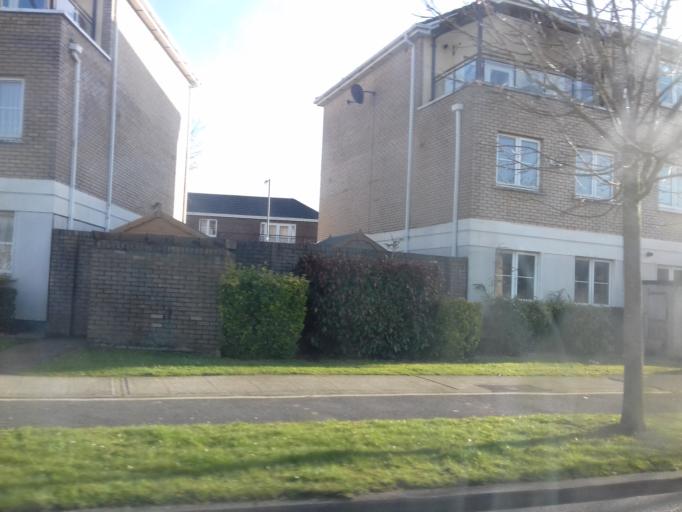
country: IE
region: Leinster
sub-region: Fingal County
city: Blanchardstown
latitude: 53.4194
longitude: -6.3872
